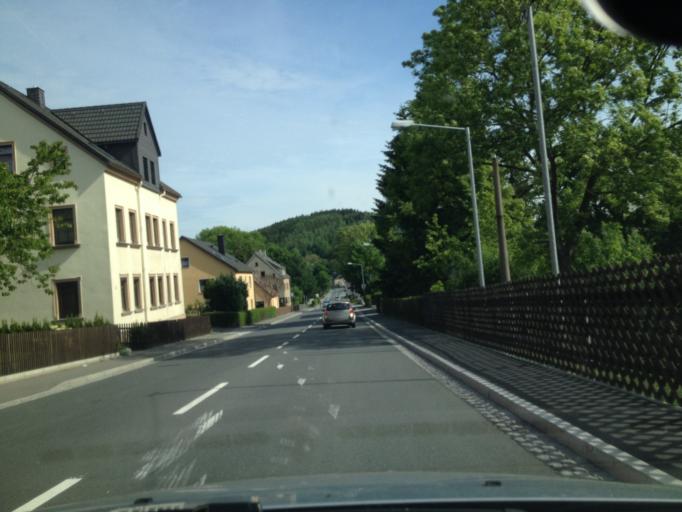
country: DE
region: Saxony
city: Ehrenfriedersdorf
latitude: 50.6512
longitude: 12.9707
